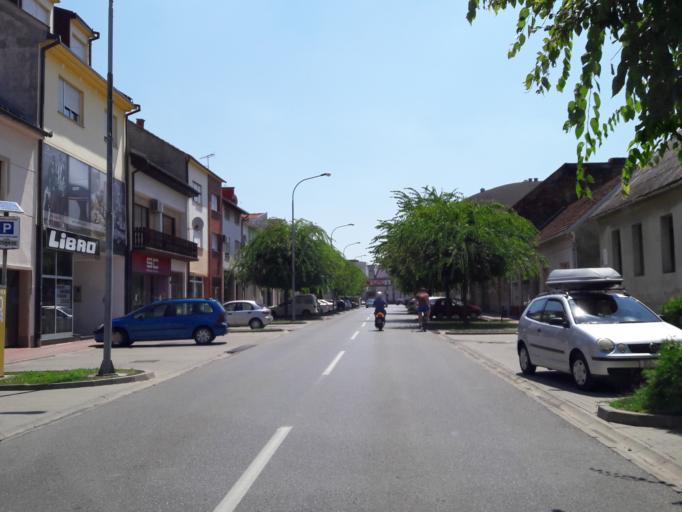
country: HR
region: Osjecko-Baranjska
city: Piskorevci
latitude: 45.3127
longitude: 18.4095
